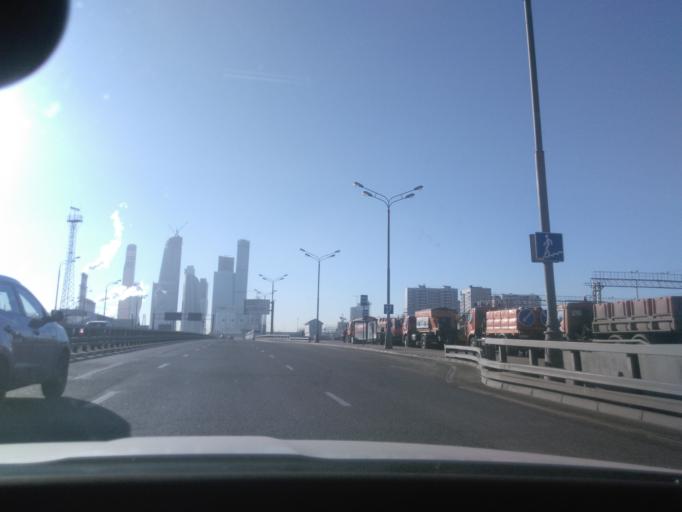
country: RU
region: Moskovskaya
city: Presnenskiy
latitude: 55.7645
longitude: 37.5201
